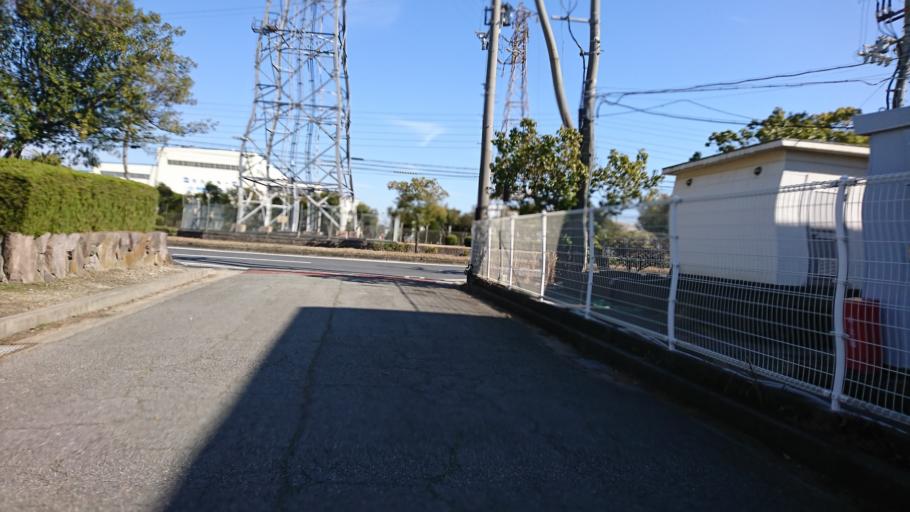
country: JP
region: Hyogo
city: Kakogawacho-honmachi
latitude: 34.7003
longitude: 134.8522
